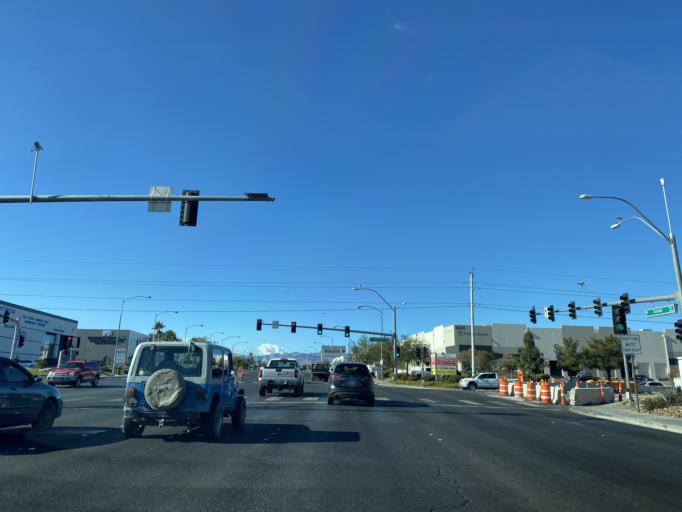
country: US
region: Nevada
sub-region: Clark County
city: Paradise
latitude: 36.0718
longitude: -115.1896
